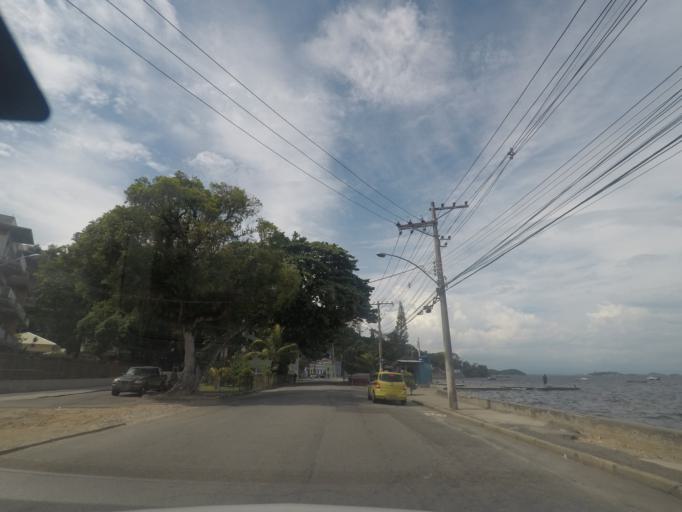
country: BR
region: Rio de Janeiro
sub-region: Rio De Janeiro
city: Rio de Janeiro
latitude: -22.8151
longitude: -43.1766
